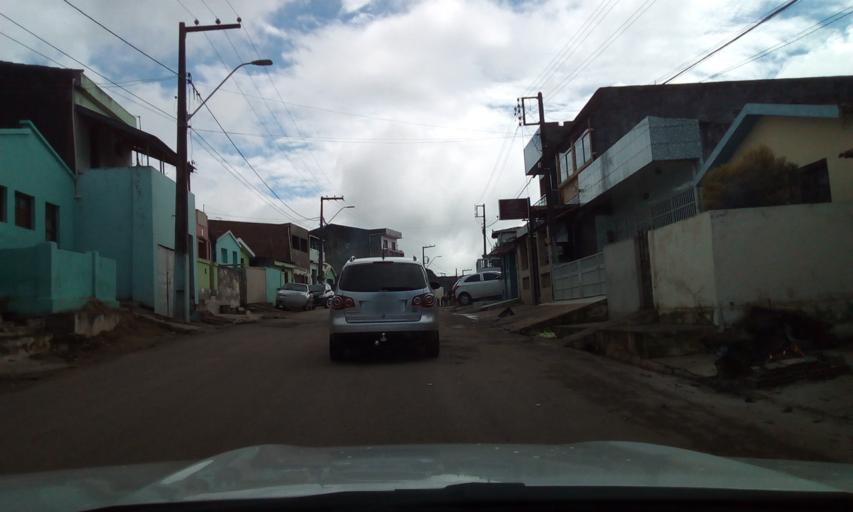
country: BR
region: Paraiba
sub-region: Areia
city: Areia
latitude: -6.9714
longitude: -35.6947
